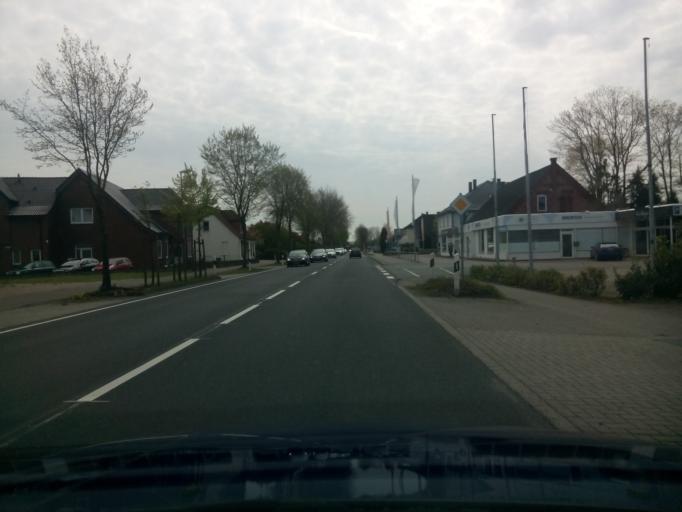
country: DE
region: Lower Saxony
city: Stuhr
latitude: 52.9912
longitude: 8.7870
